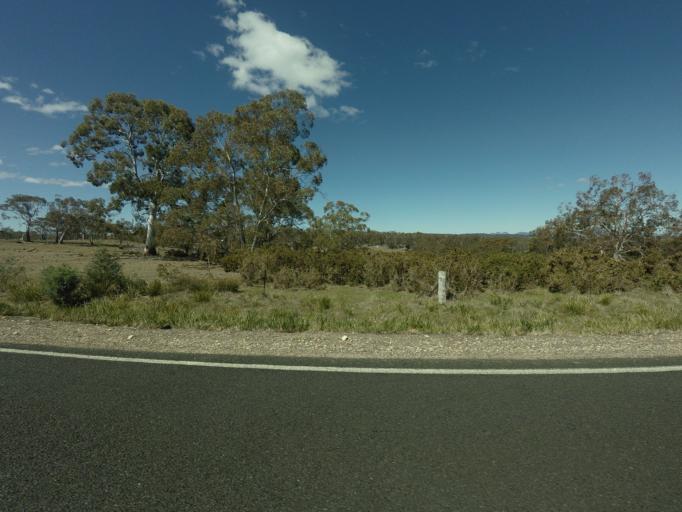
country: AU
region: Tasmania
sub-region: Break O'Day
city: St Helens
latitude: -42.0281
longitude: 148.0184
